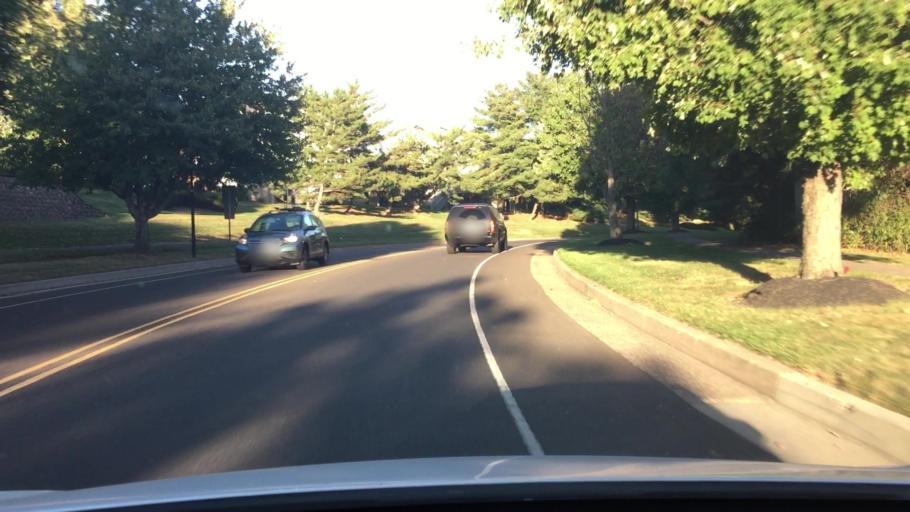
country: US
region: Pennsylvania
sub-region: Bucks County
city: Newtown
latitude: 40.2166
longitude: -74.9471
